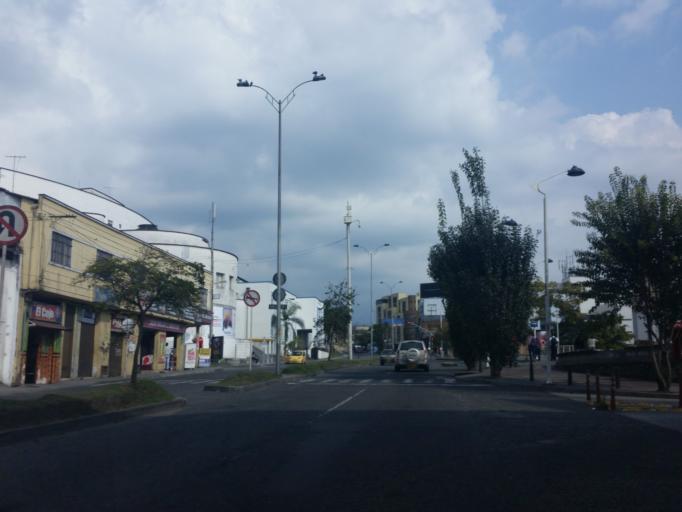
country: CO
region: Caldas
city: Manizales
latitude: 5.0637
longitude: -75.5008
